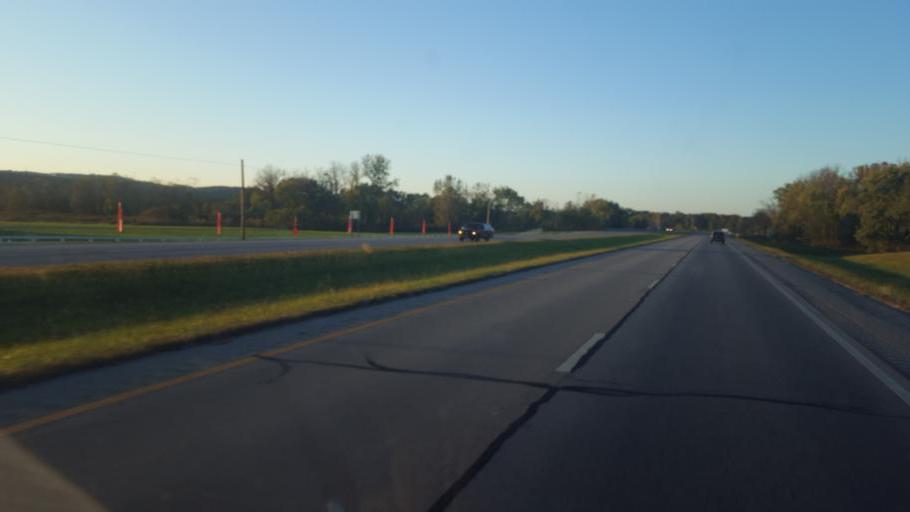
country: US
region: Ohio
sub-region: Pike County
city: Piketon
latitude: 38.9781
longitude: -83.0227
